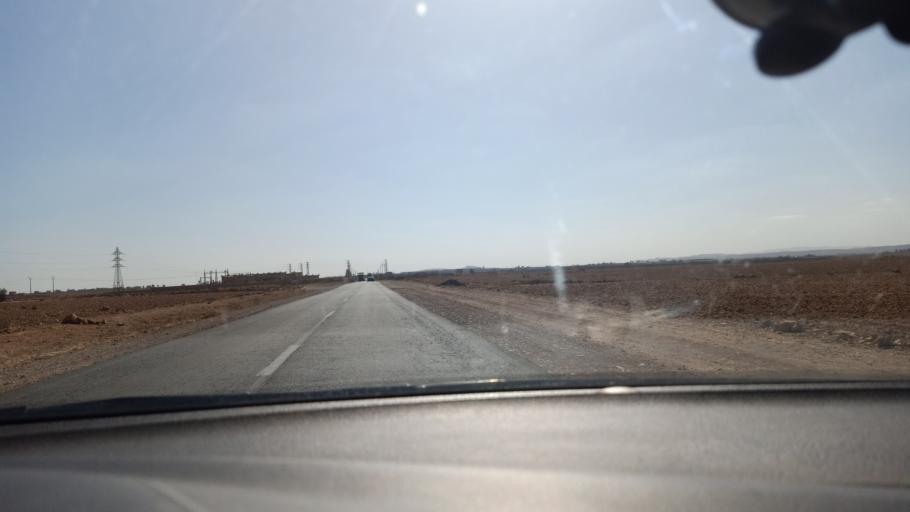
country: MA
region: Doukkala-Abda
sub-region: Safi
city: Youssoufia
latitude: 32.1138
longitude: -8.6070
